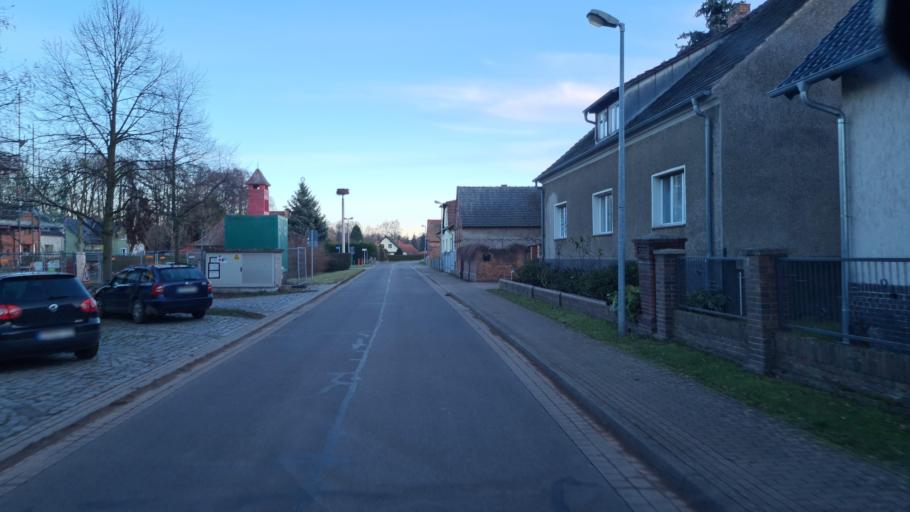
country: DE
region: Brandenburg
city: Burg
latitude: 51.8127
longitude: 14.1349
